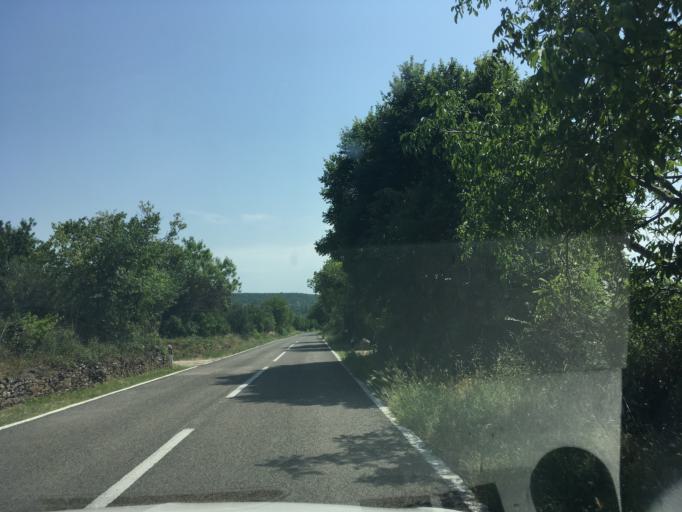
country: HR
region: Sibensko-Kniniska
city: Kistanje
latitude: 43.9354
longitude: 15.8340
